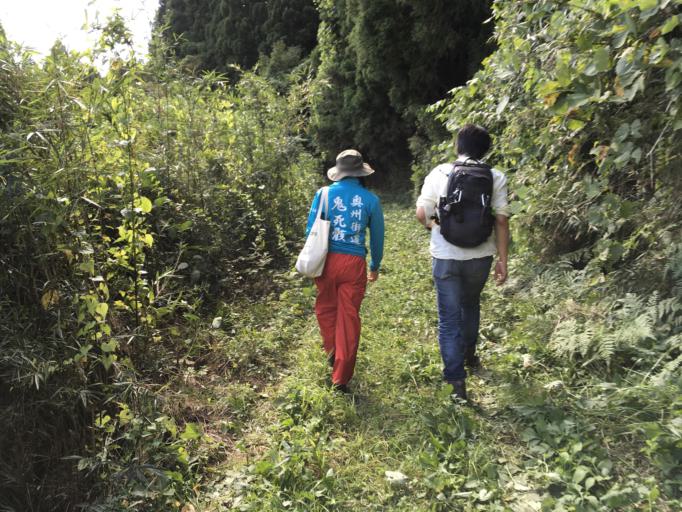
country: JP
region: Iwate
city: Ichinoseki
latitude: 38.8872
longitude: 141.1256
